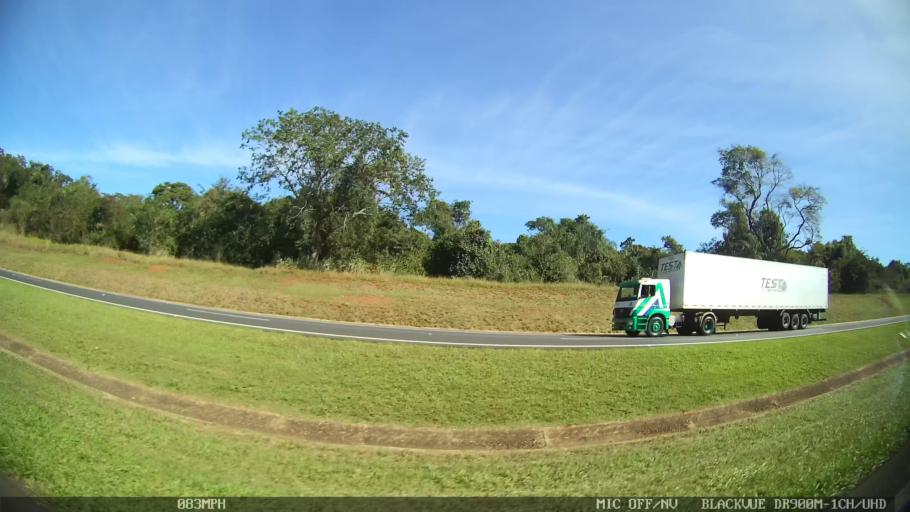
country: BR
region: Sao Paulo
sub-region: Pirassununga
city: Pirassununga
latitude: -21.9426
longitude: -47.4647
